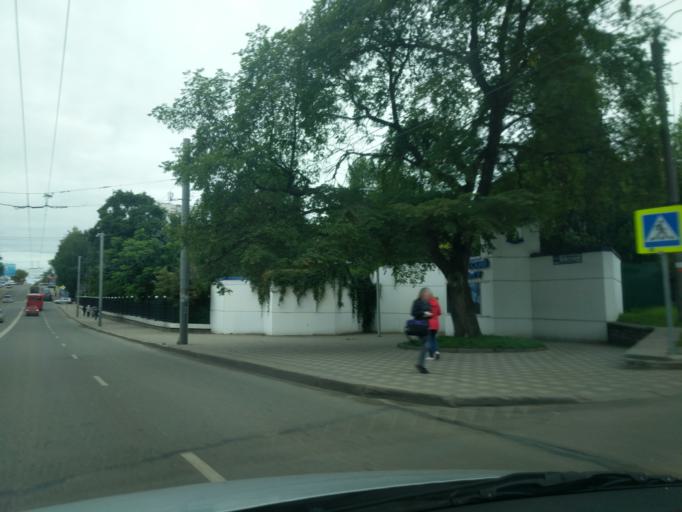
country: RU
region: Kirov
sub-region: Kirovo-Chepetskiy Rayon
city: Kirov
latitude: 58.5974
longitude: 49.6685
